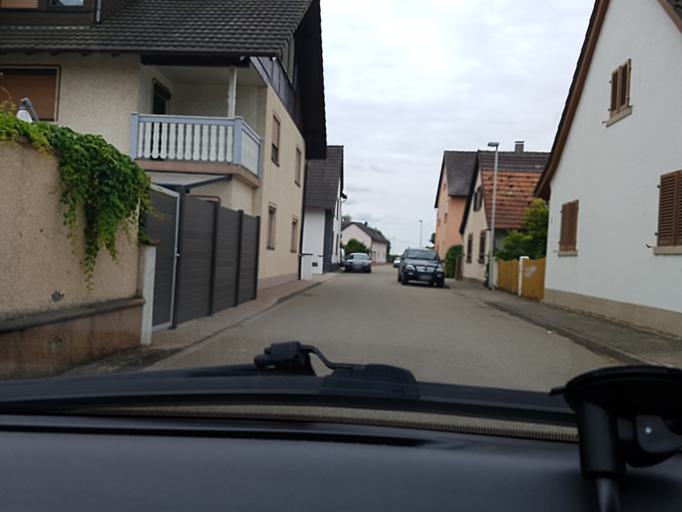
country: DE
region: Baden-Wuerttemberg
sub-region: Freiburg Region
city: Willstatt
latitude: 48.5564
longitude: 7.8853
